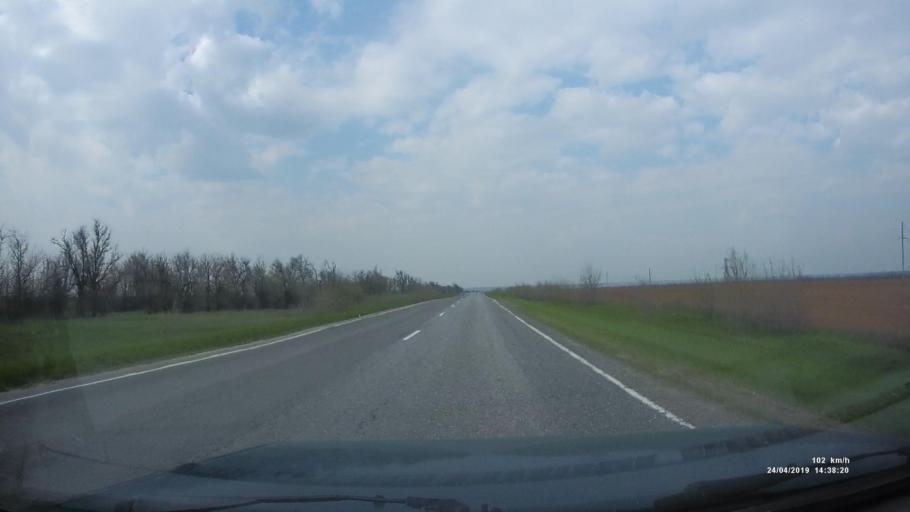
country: RU
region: Rostov
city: Remontnoye
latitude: 46.3992
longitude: 43.8861
